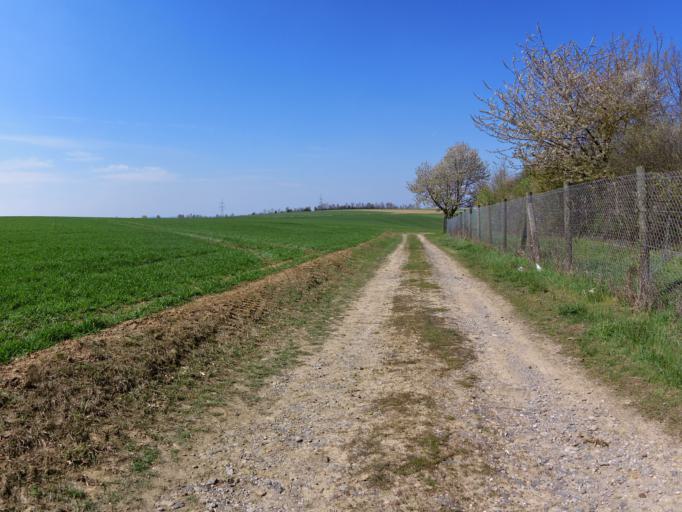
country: DE
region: Bavaria
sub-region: Regierungsbezirk Unterfranken
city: Biebelried
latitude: 49.7850
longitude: 10.0690
